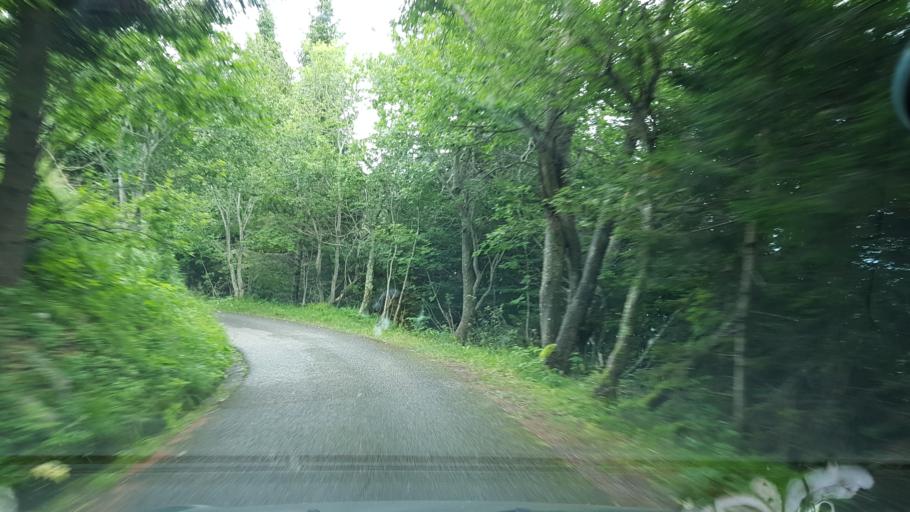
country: IT
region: Friuli Venezia Giulia
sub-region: Provincia di Udine
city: Cercivento
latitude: 46.5480
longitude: 12.9820
